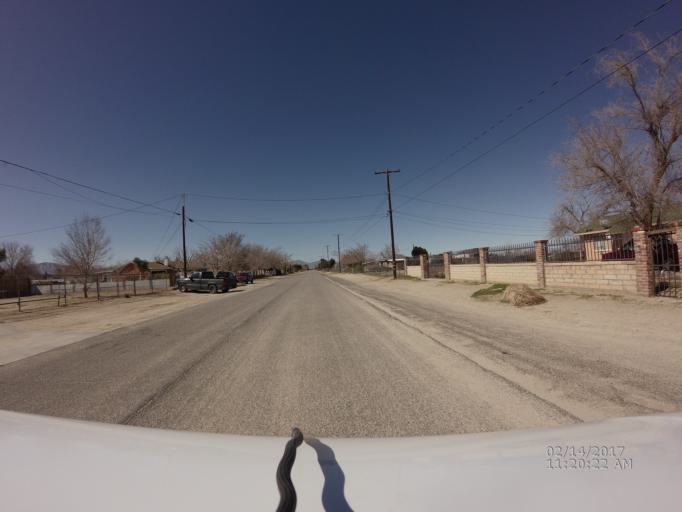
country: US
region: California
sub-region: Los Angeles County
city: Littlerock
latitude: 34.5596
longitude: -117.9622
